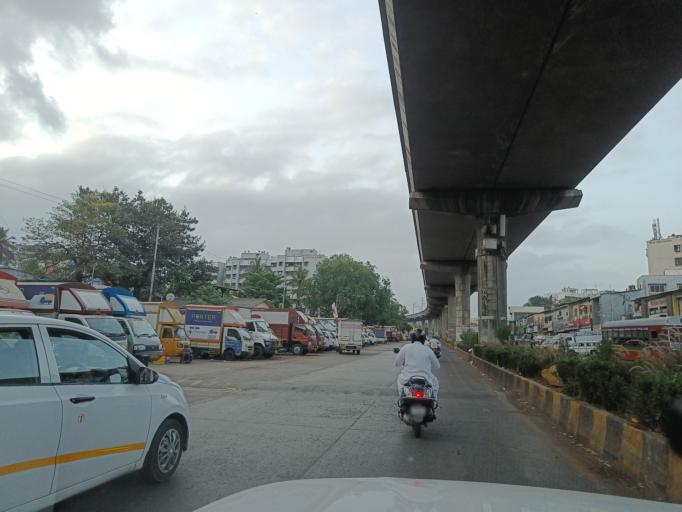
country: IN
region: Maharashtra
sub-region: Mumbai Suburban
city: Powai
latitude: 19.0999
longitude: 72.8918
